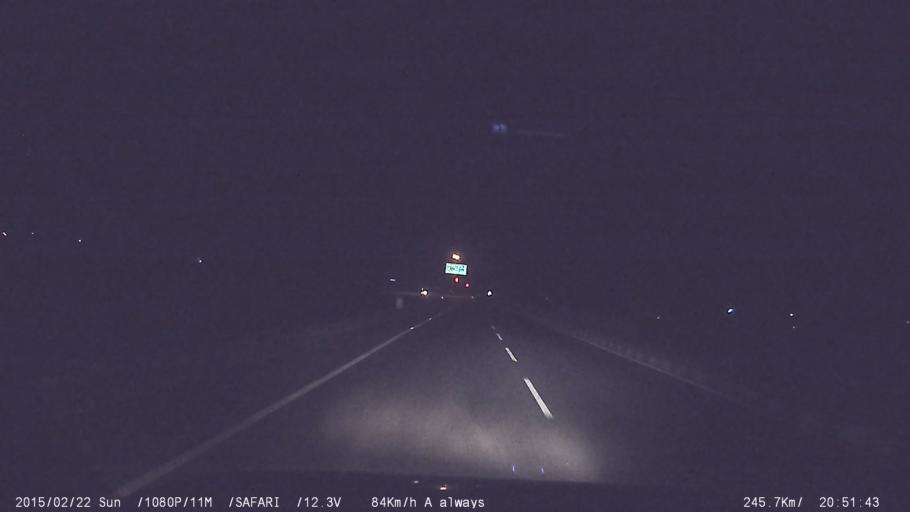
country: IN
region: Tamil Nadu
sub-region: Dindigul
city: Vedasandur
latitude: 10.5460
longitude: 77.9432
